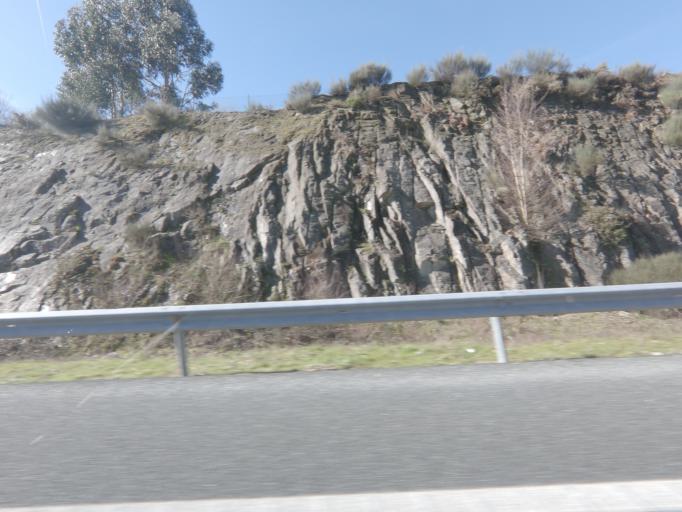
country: ES
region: Galicia
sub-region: Provincia de Ourense
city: Pinor
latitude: 42.4903
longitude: -8.0242
